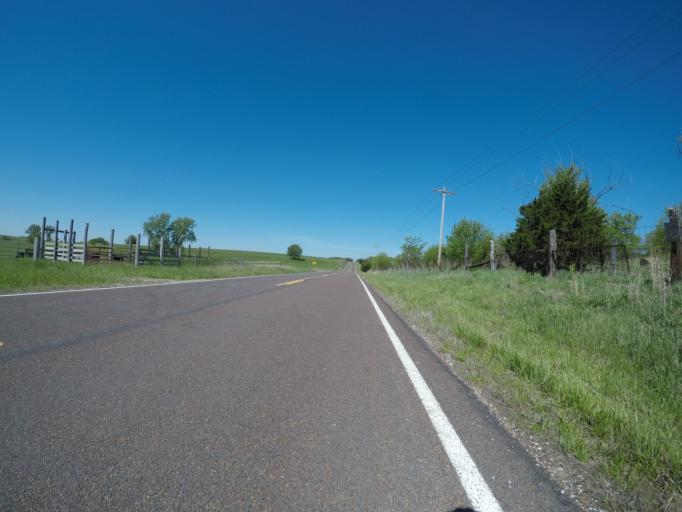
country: US
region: Kansas
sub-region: Osage County
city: Overbrook
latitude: 38.8405
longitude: -95.4912
